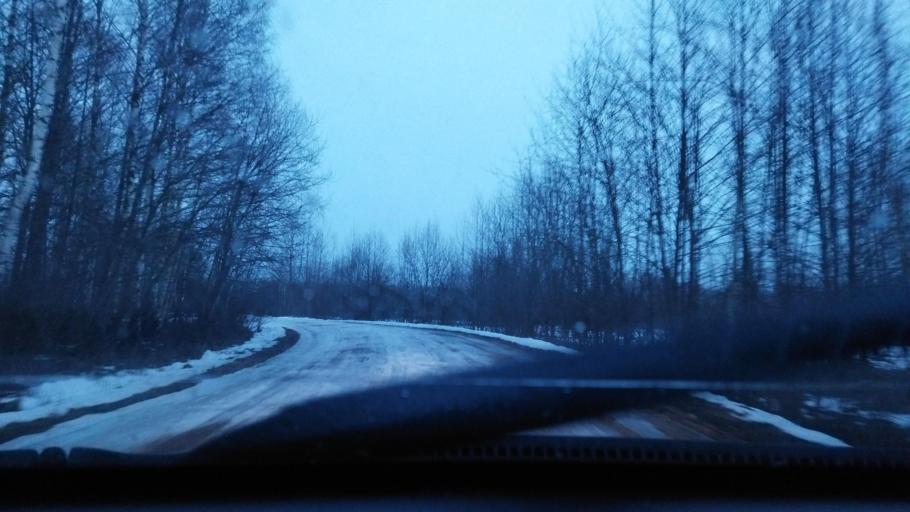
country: BY
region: Minsk
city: Svir
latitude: 54.9375
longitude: 26.3933
